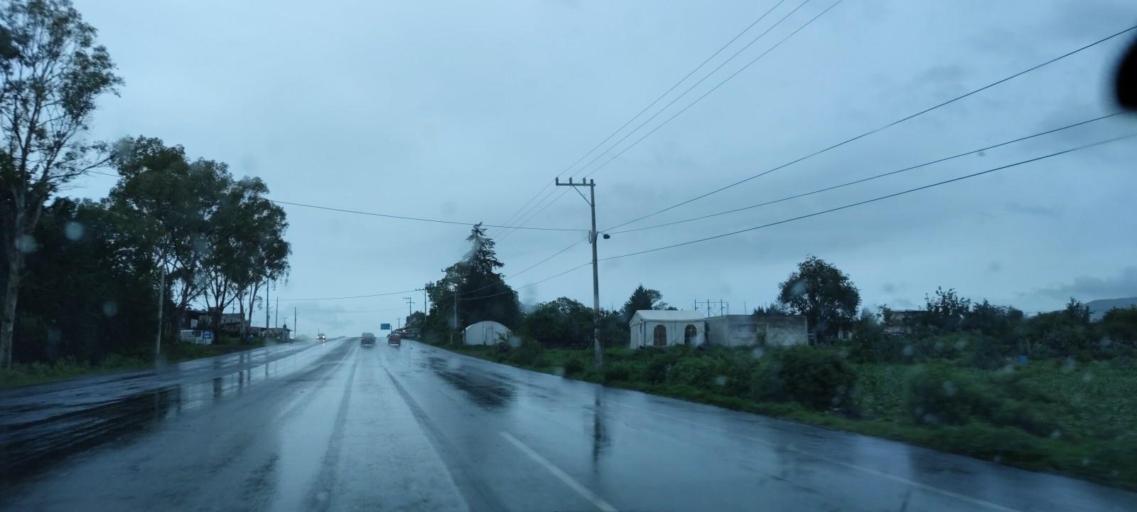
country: MX
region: Mexico
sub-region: Jilotepec
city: Doxhicho
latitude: 19.9241
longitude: -99.5858
